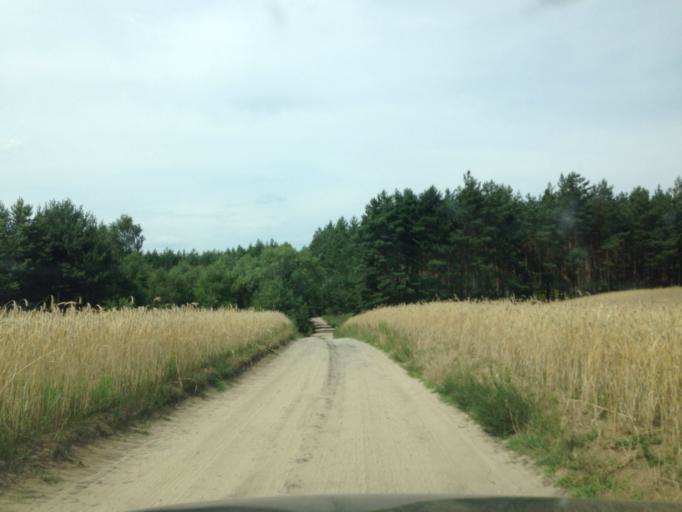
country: PL
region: Kujawsko-Pomorskie
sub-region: Powiat brodnicki
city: Bartniczka
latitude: 53.2724
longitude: 19.5155
